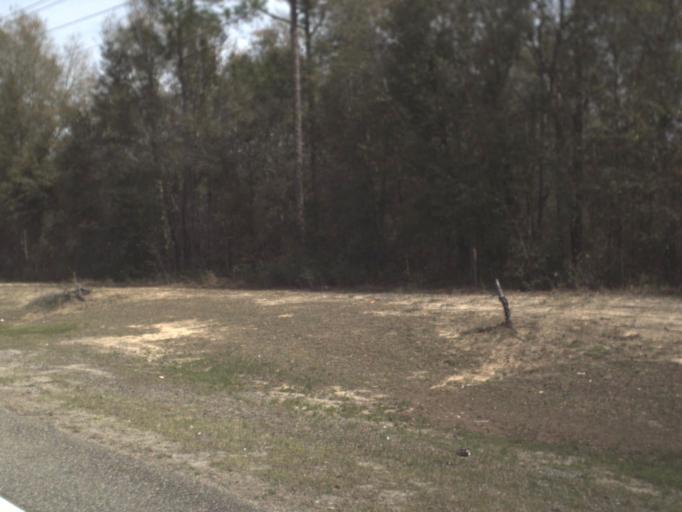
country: US
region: Florida
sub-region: Leon County
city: Tallahassee
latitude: 30.4129
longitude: -84.3530
